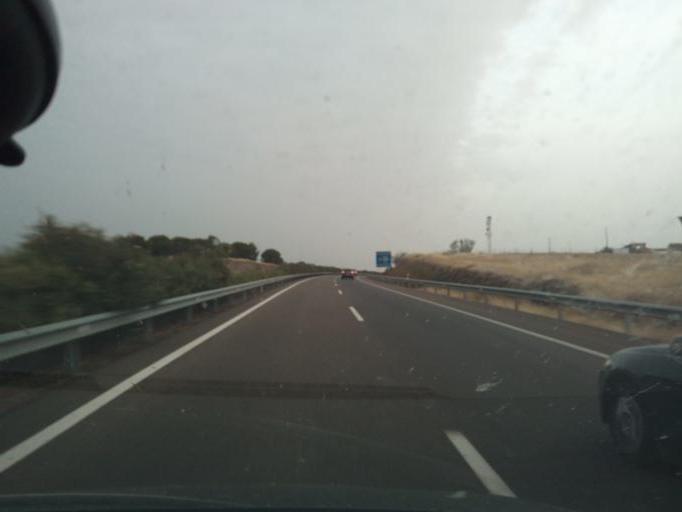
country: ES
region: Extremadura
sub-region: Provincia de Badajoz
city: Trujillanos
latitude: 38.9494
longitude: -6.2551
